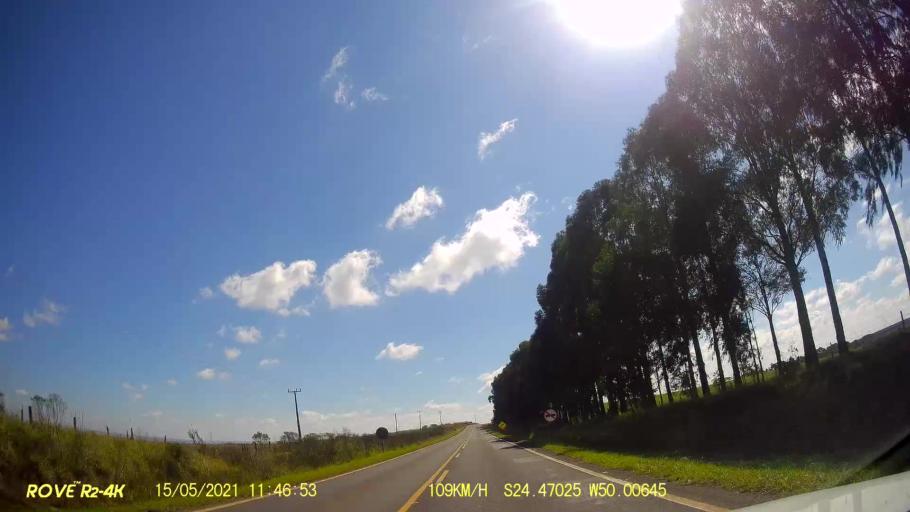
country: BR
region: Parana
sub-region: Pirai Do Sul
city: Pirai do Sul
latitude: -24.4702
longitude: -50.0065
